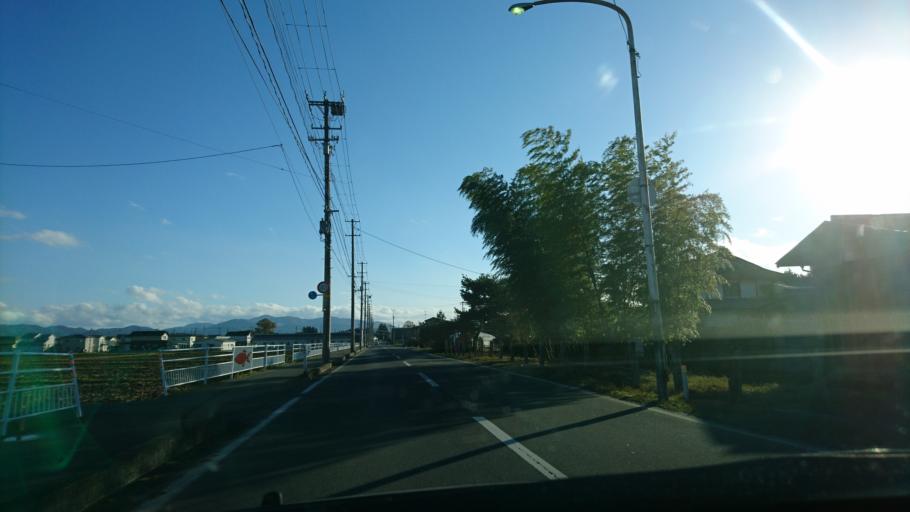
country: JP
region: Iwate
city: Mizusawa
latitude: 39.1228
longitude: 141.1556
